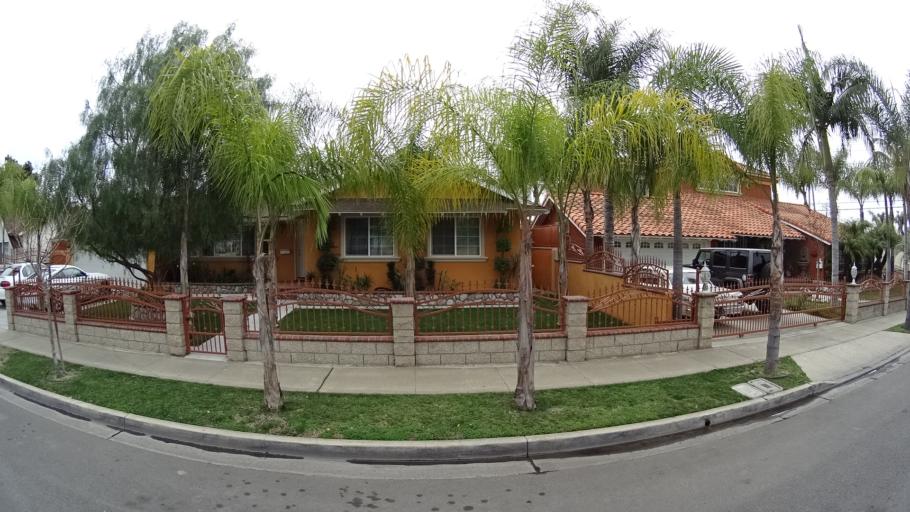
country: US
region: California
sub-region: Orange County
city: Stanton
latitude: 33.8215
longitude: -117.9794
